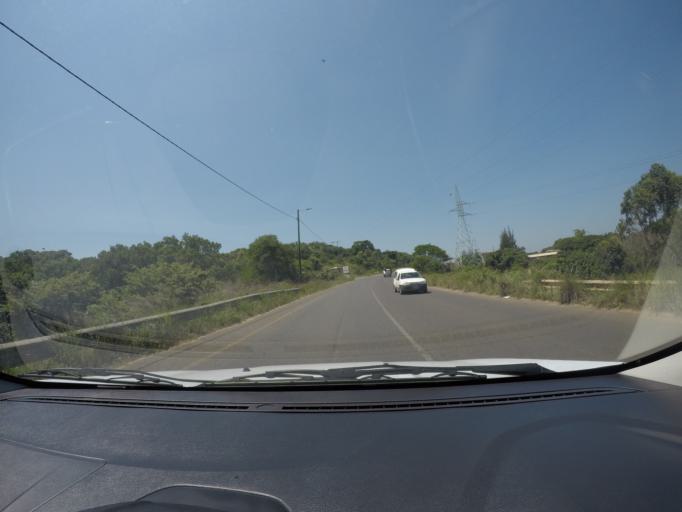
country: ZA
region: KwaZulu-Natal
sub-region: uThungulu District Municipality
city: eSikhawini
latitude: -28.8536
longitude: 31.9234
